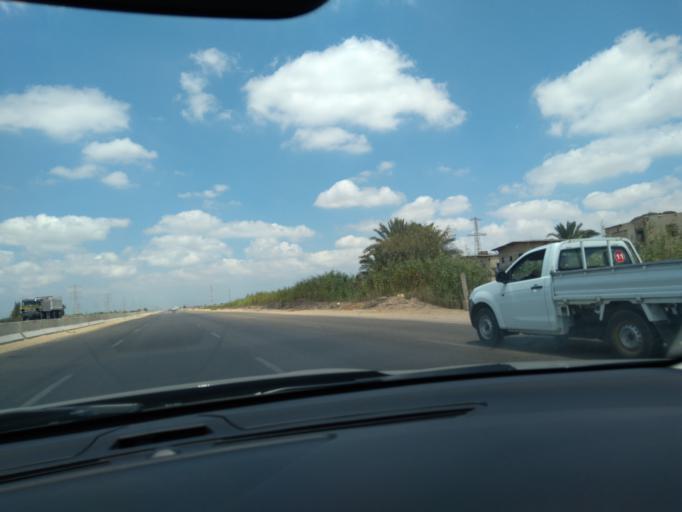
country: EG
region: Muhafazat Bur Sa`id
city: Port Said
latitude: 31.0389
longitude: 32.3060
